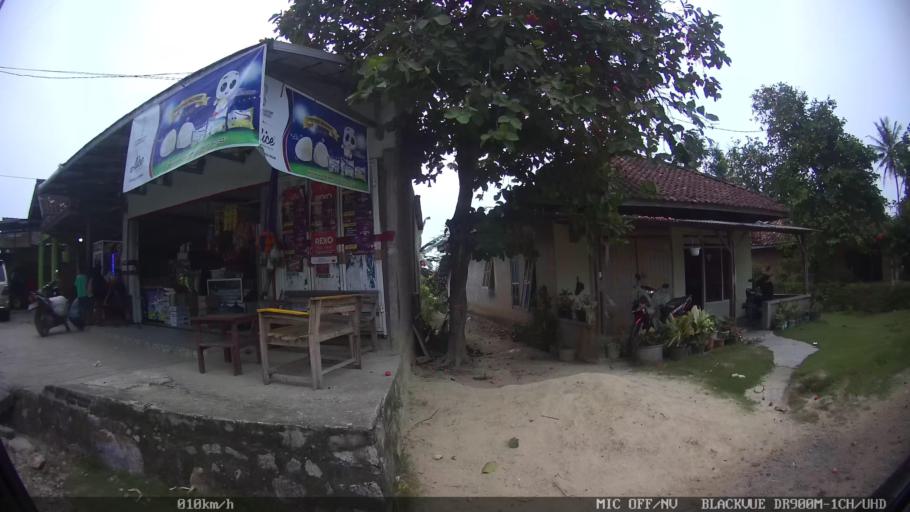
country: ID
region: Lampung
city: Panjang
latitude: -5.4210
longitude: 105.3503
